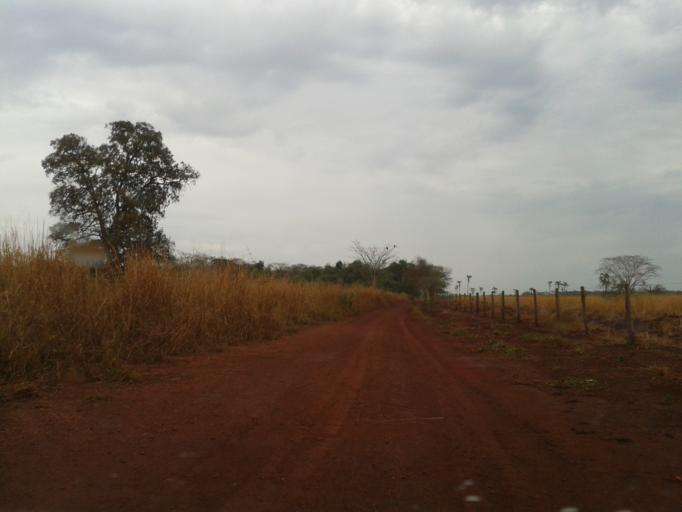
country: BR
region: Minas Gerais
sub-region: Capinopolis
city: Capinopolis
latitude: -18.8733
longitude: -49.7907
